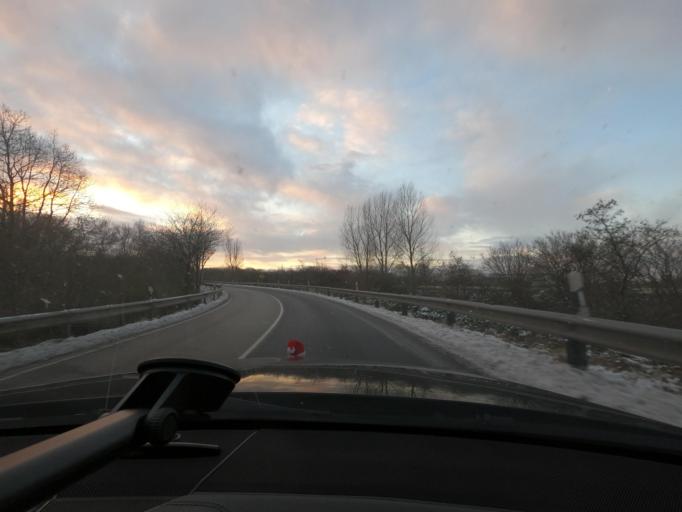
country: DE
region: Schleswig-Holstein
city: Flensburg
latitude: 54.7683
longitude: 9.4194
